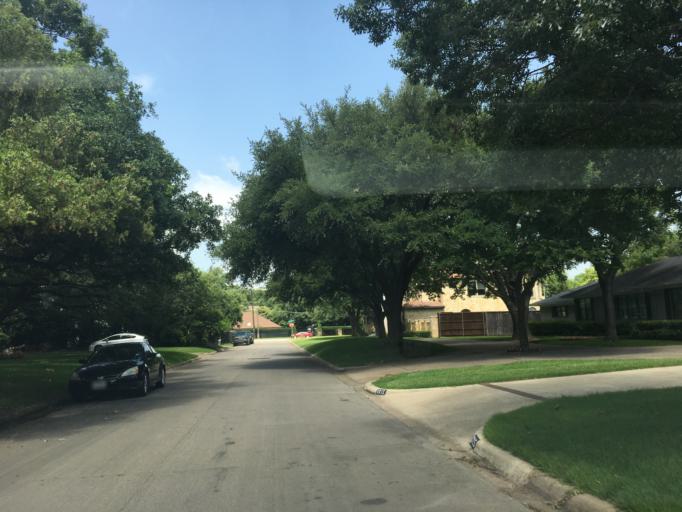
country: US
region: Texas
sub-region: Dallas County
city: University Park
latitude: 32.8792
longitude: -96.8026
